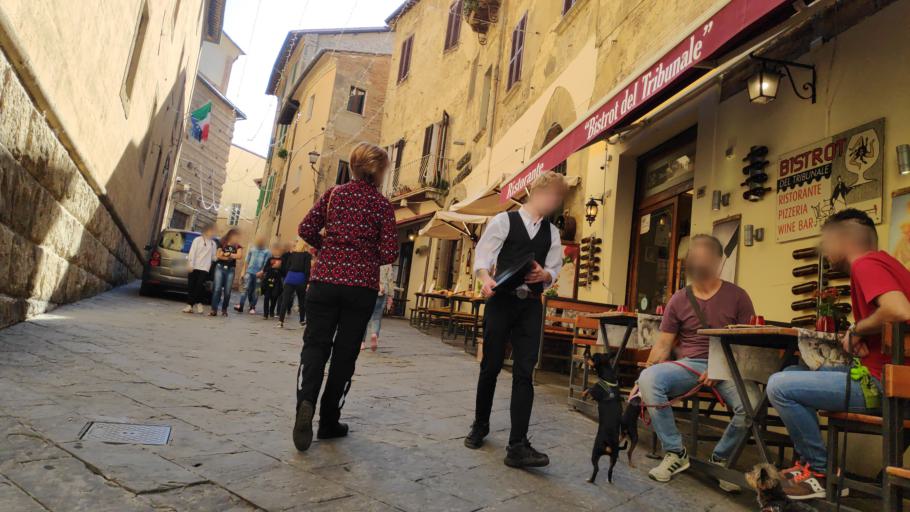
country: IT
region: Tuscany
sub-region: Provincia di Siena
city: Montepulciano
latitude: 43.0933
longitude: 11.7821
